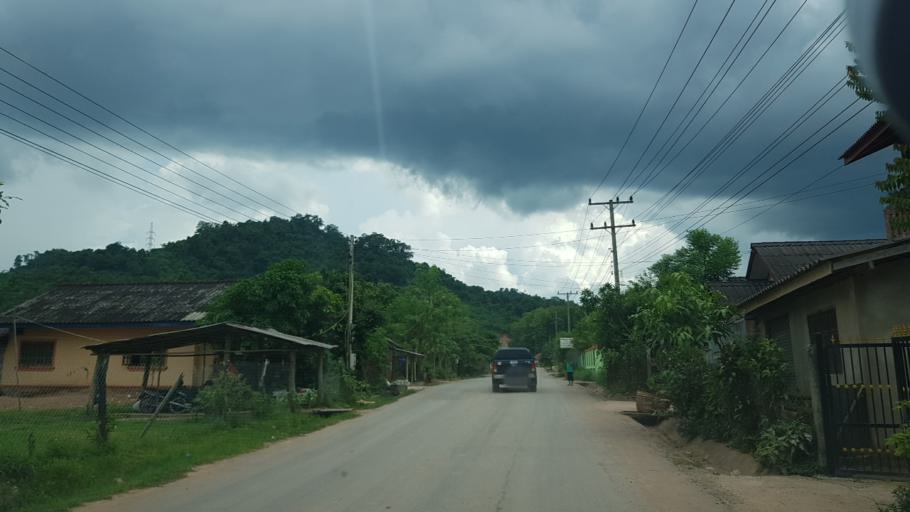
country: LA
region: Oudomxai
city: Muang Xay
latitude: 20.6717
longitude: 101.9669
